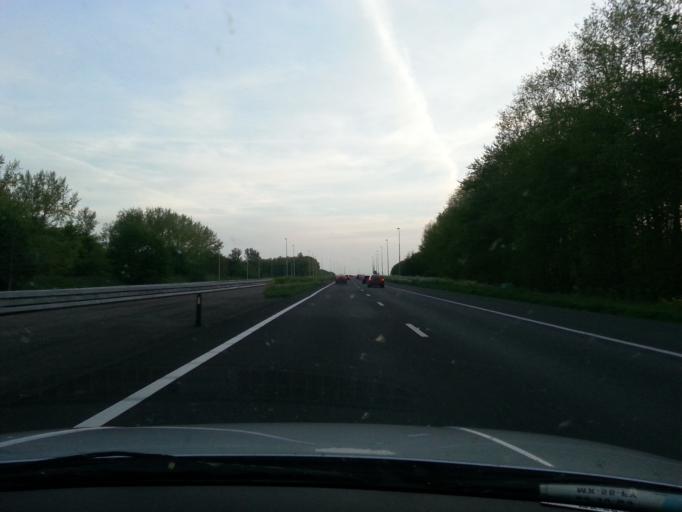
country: NL
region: Flevoland
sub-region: Gemeente Lelystad
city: Lelystad
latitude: 52.4843
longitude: 5.5113
